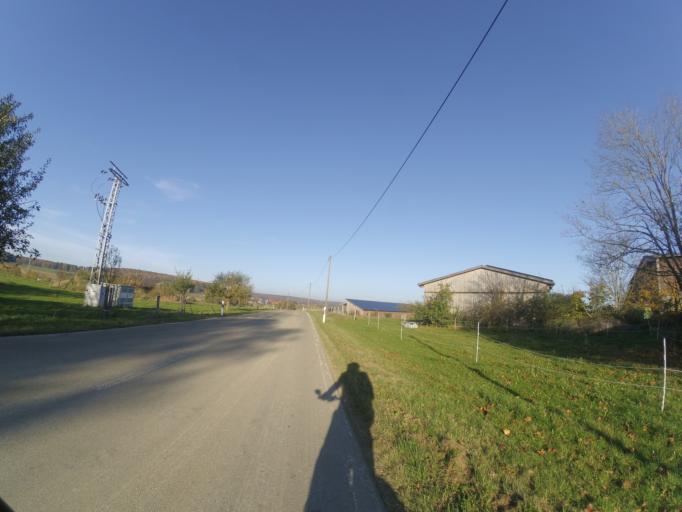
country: DE
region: Baden-Wuerttemberg
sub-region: Tuebingen Region
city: Berghulen
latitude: 48.4701
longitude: 9.7848
